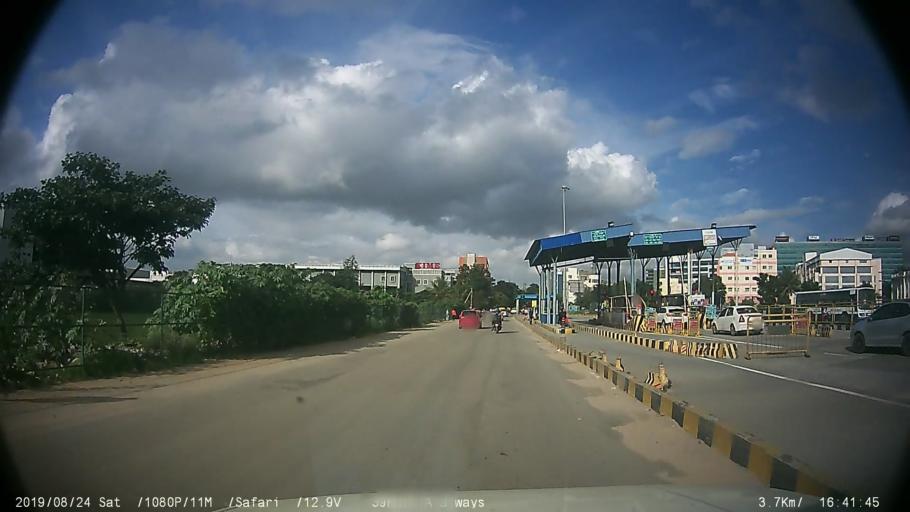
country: IN
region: Karnataka
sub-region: Bangalore Urban
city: Anekal
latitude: 12.8470
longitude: 77.6735
